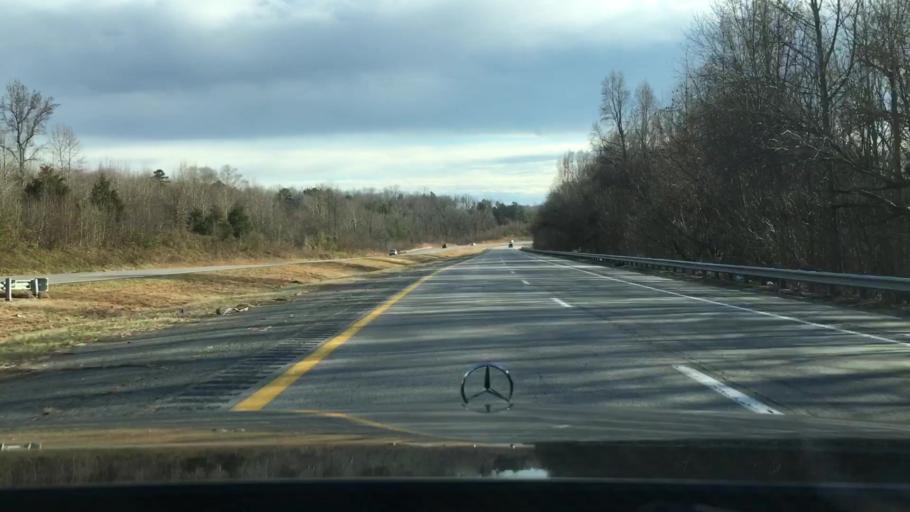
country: US
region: Virginia
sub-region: City of Danville
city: Danville
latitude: 36.6074
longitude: -79.3581
